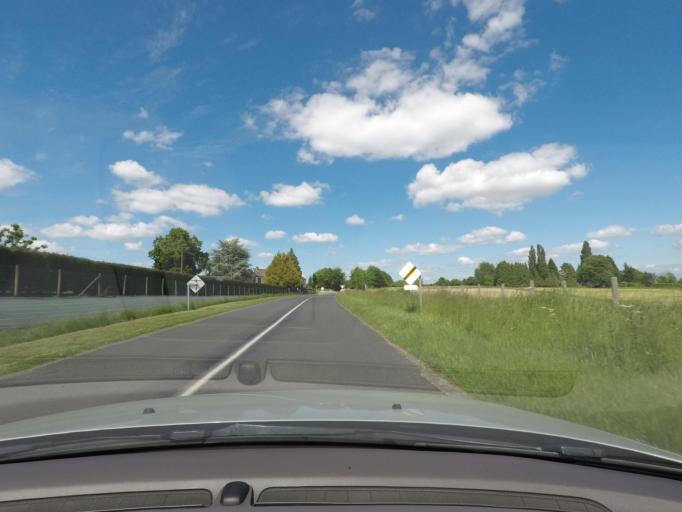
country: FR
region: Lower Normandy
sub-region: Departement de l'Orne
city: Mortagne-au-Perche
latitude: 48.5419
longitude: 0.5643
